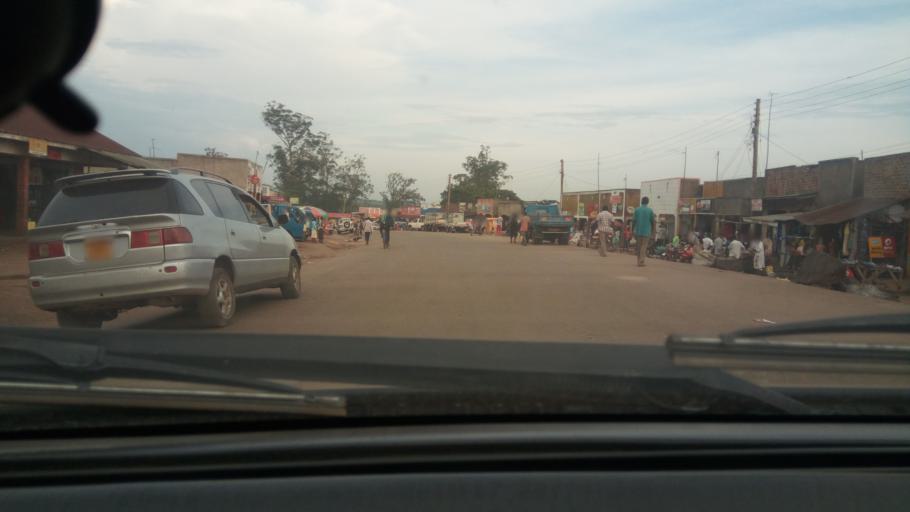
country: UG
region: Central Region
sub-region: Mityana District
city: Mityana
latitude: 0.5659
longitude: 32.2036
